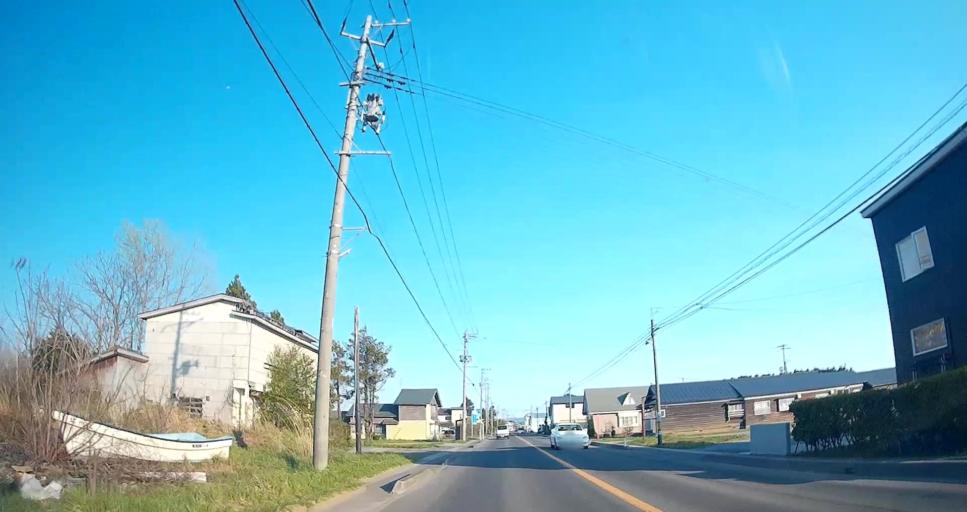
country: JP
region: Aomori
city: Mutsu
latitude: 41.2764
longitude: 141.2130
